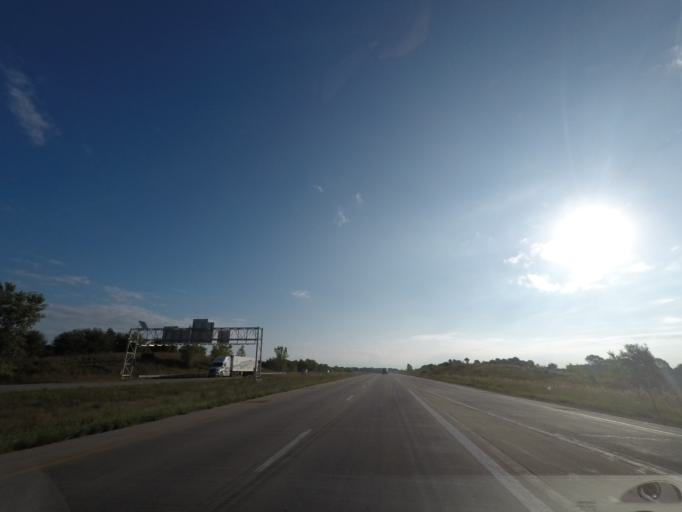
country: US
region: Iowa
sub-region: Warren County
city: Carlisle
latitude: 41.5077
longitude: -93.5652
